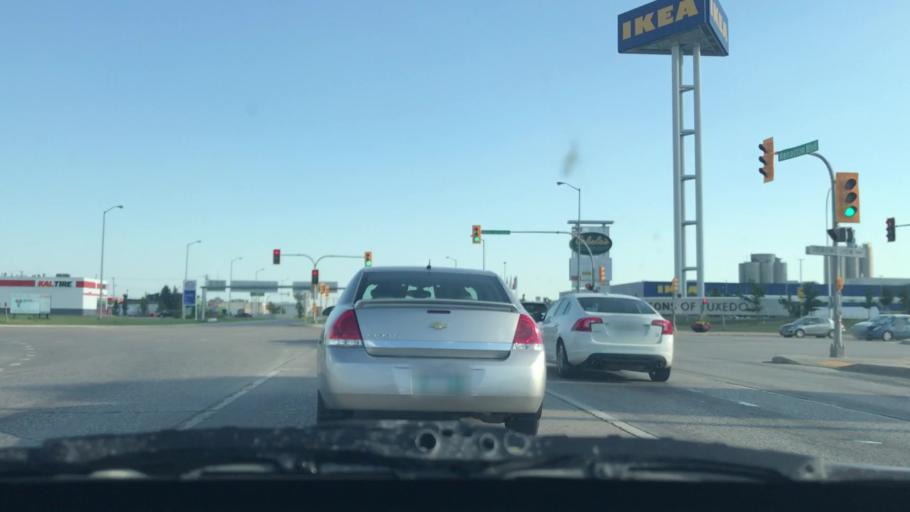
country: CA
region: Manitoba
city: Winnipeg
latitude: 49.8420
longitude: -97.2089
